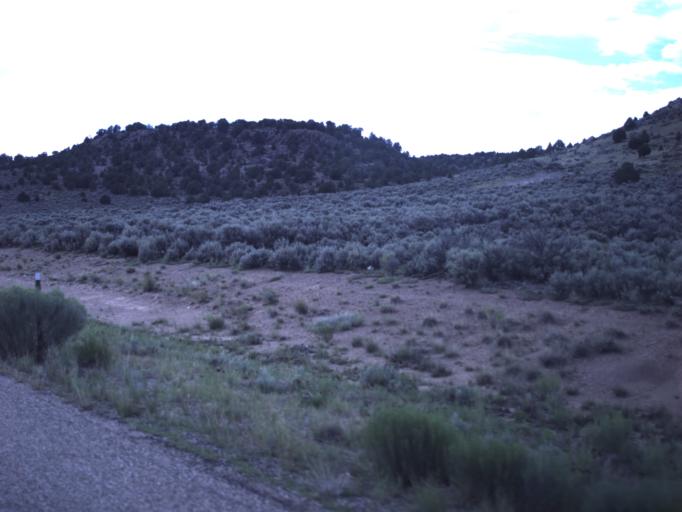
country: US
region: Utah
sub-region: Garfield County
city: Panguitch
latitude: 37.9664
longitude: -112.4241
